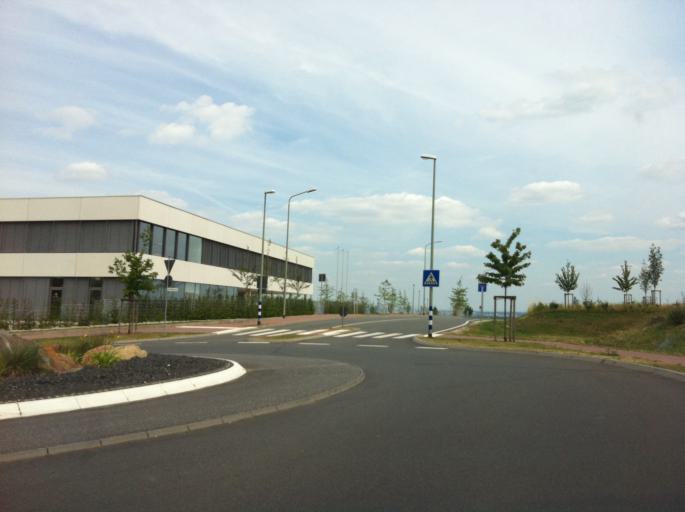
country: DE
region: Hesse
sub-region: Regierungsbezirk Darmstadt
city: Bad Soden am Taunus
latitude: 50.1339
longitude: 8.4956
